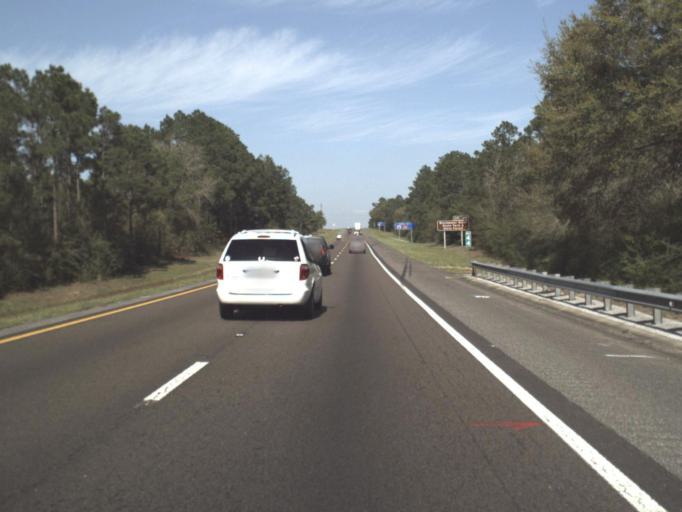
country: US
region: Florida
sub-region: Okaloosa County
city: Crestview
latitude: 30.6924
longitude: -86.7674
